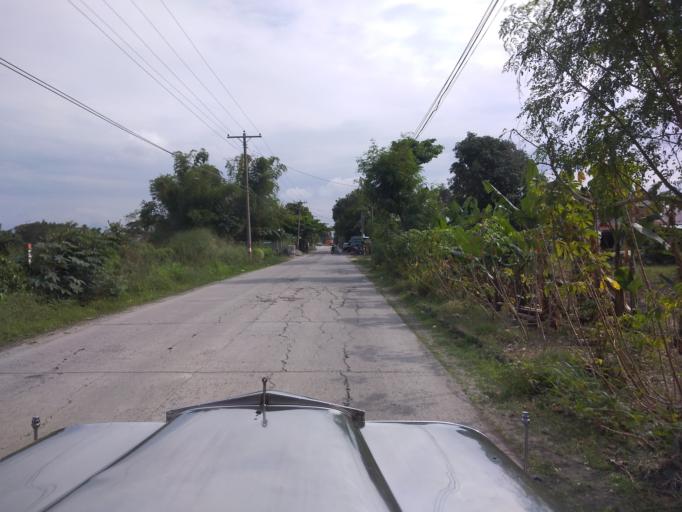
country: PH
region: Central Luzon
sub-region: Province of Pampanga
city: San Patricio
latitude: 15.0970
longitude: 120.7105
